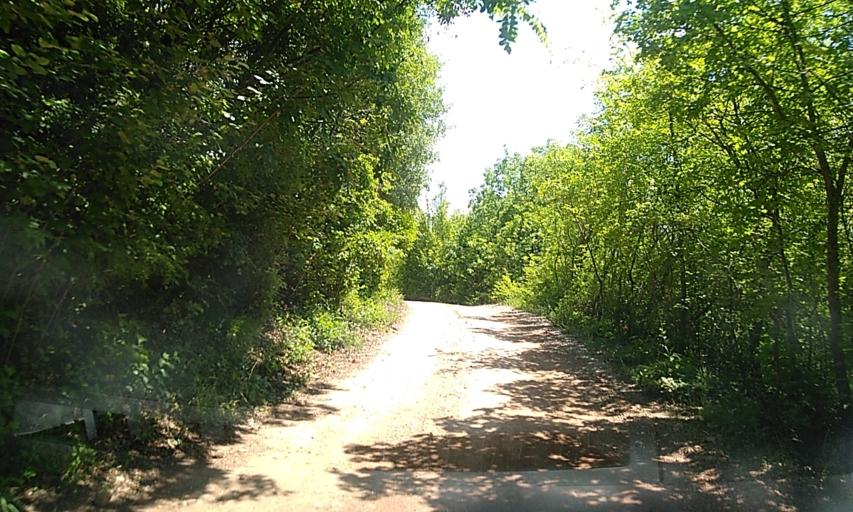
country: RS
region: Central Serbia
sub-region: Nisavski Okrug
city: Niska Banja
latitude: 43.3711
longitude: 21.9924
